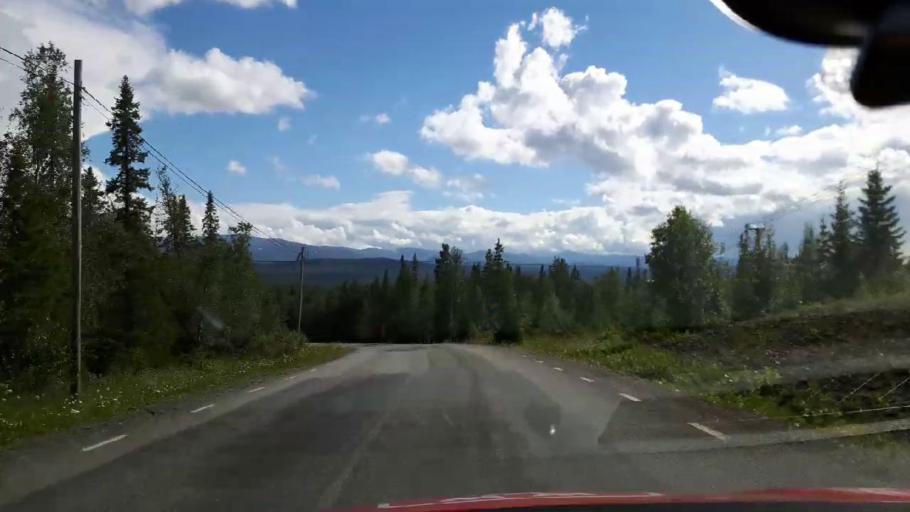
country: SE
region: Jaemtland
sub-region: Are Kommun
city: Are
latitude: 63.2283
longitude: 13.1594
